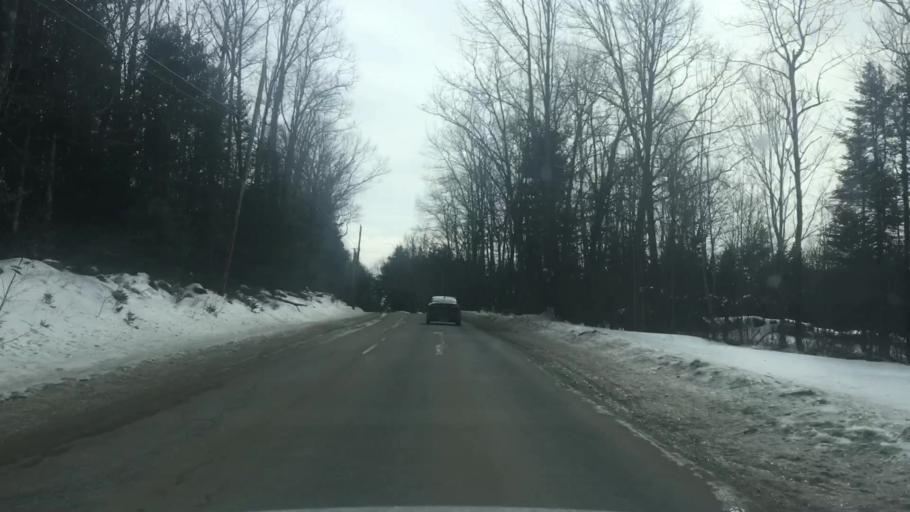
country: US
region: Maine
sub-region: Hancock County
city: Orland
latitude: 44.5851
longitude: -68.7258
